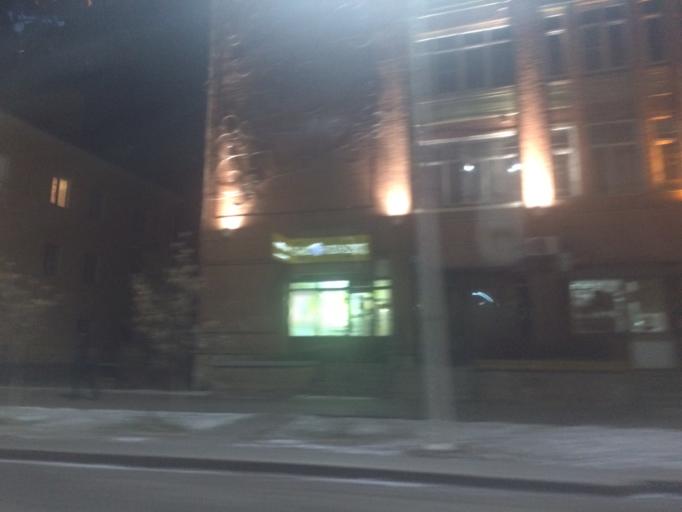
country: KZ
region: Astana Qalasy
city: Astana
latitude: 51.1837
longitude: 71.4167
